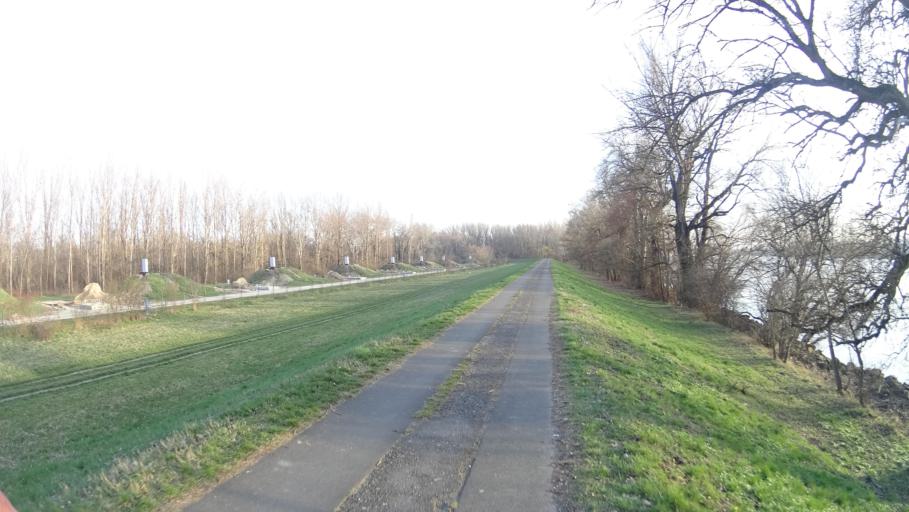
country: HU
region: Pest
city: God
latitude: 47.6996
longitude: 19.1293
